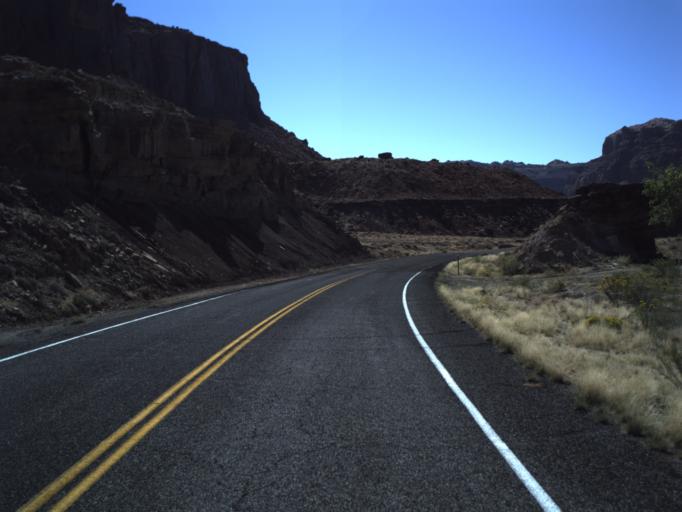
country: US
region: Utah
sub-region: San Juan County
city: Blanding
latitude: 37.9306
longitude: -110.4650
